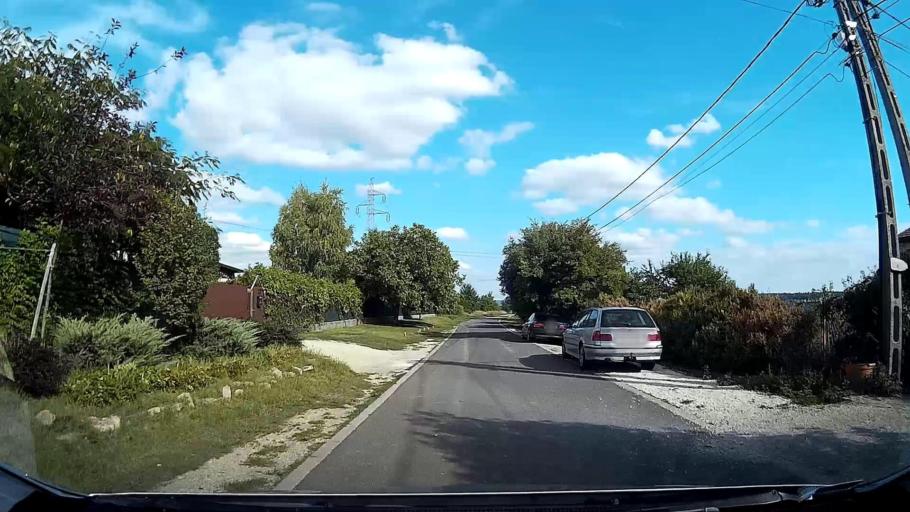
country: HU
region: Pest
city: Pomaz
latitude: 47.6331
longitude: 19.0219
